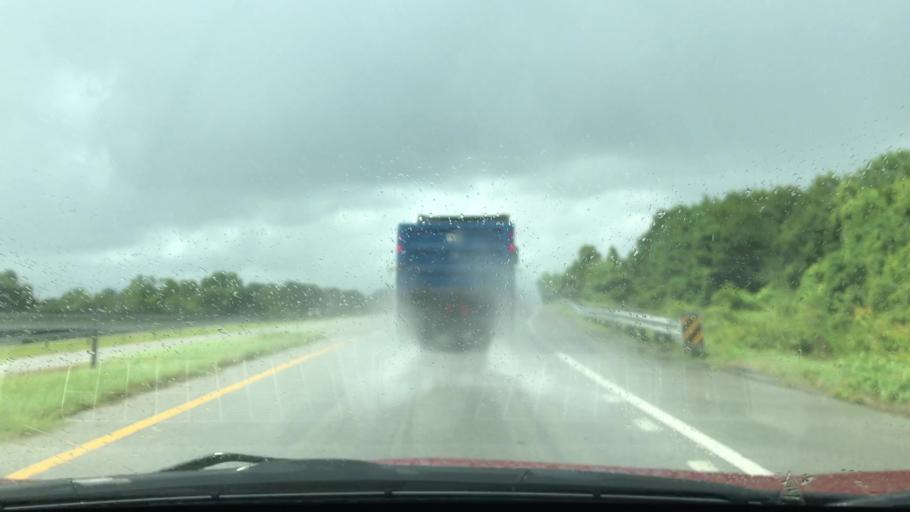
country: US
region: South Carolina
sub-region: Charleston County
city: Mount Pleasant
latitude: 32.8222
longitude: -79.8489
